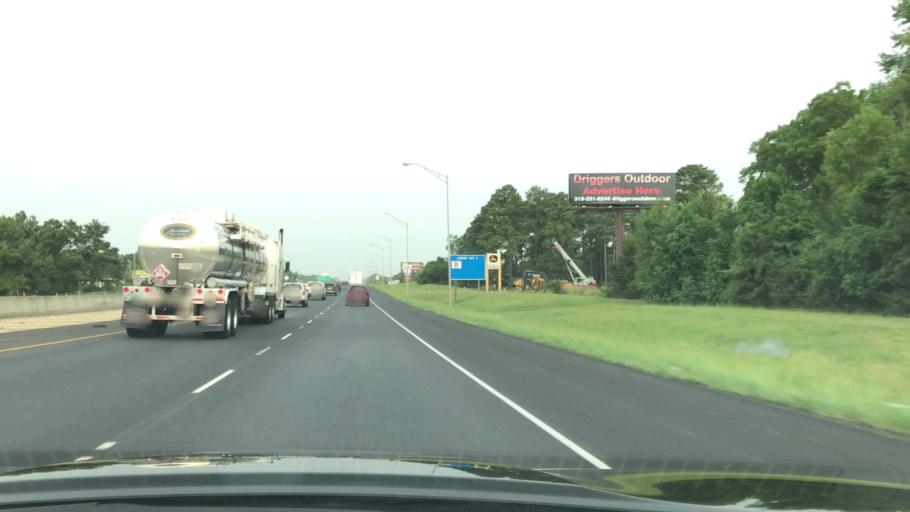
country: US
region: Louisiana
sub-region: Caddo Parish
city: Greenwood
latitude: 32.4496
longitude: -93.8785
